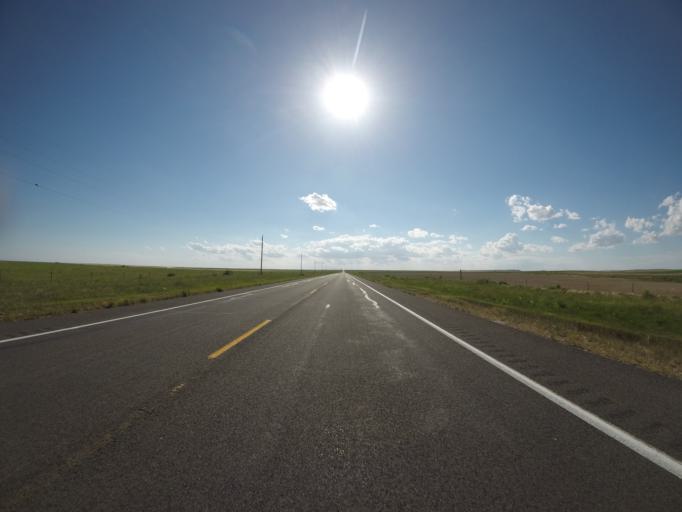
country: US
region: Colorado
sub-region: Morgan County
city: Fort Morgan
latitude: 40.6104
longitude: -103.7384
